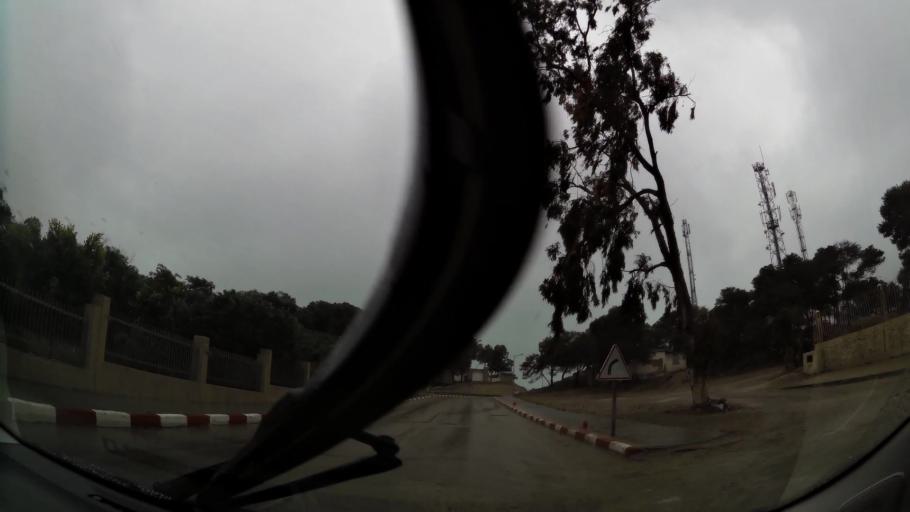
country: MA
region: Taza-Al Hoceima-Taounate
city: Al Hoceima
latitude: 35.2491
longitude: -3.9430
